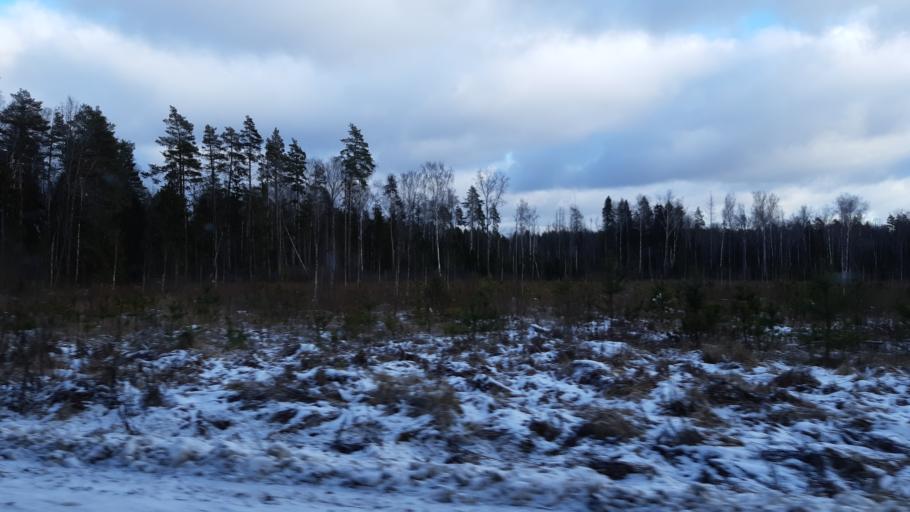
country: RU
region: Moskovskaya
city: Noginsk-9
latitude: 55.9696
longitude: 38.5370
